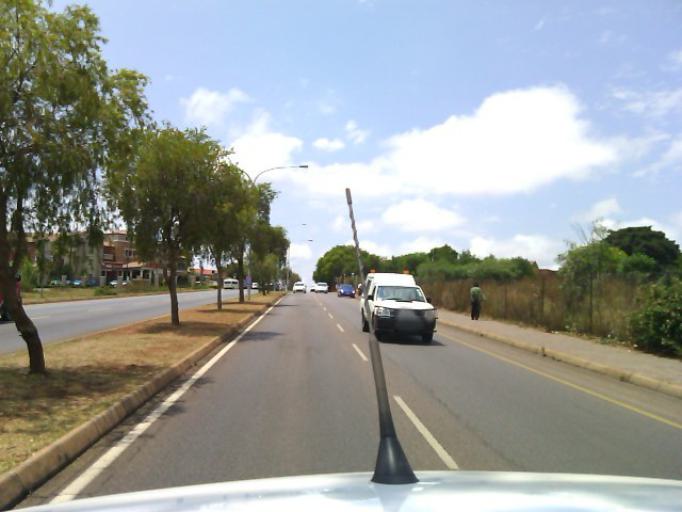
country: ZA
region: Gauteng
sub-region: City of Tshwane Metropolitan Municipality
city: Centurion
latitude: -25.8359
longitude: 28.1931
